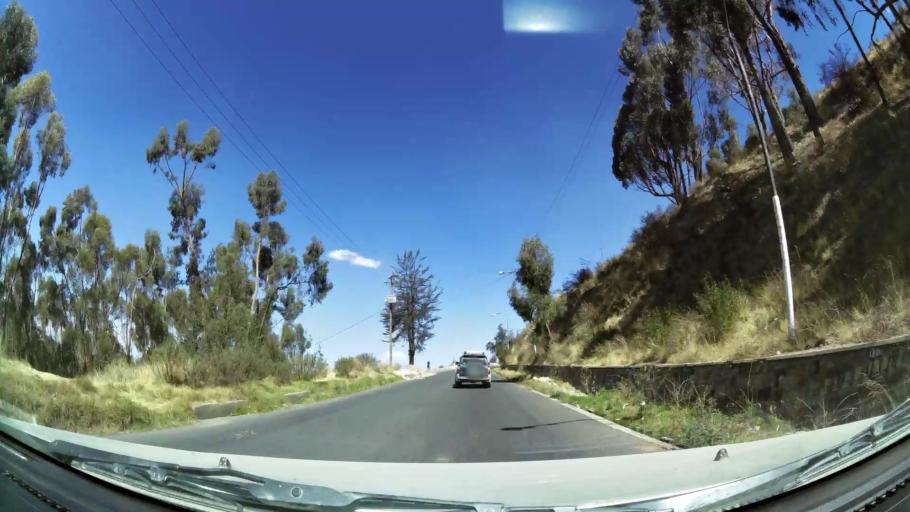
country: BO
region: La Paz
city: La Paz
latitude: -16.4847
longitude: -68.1552
